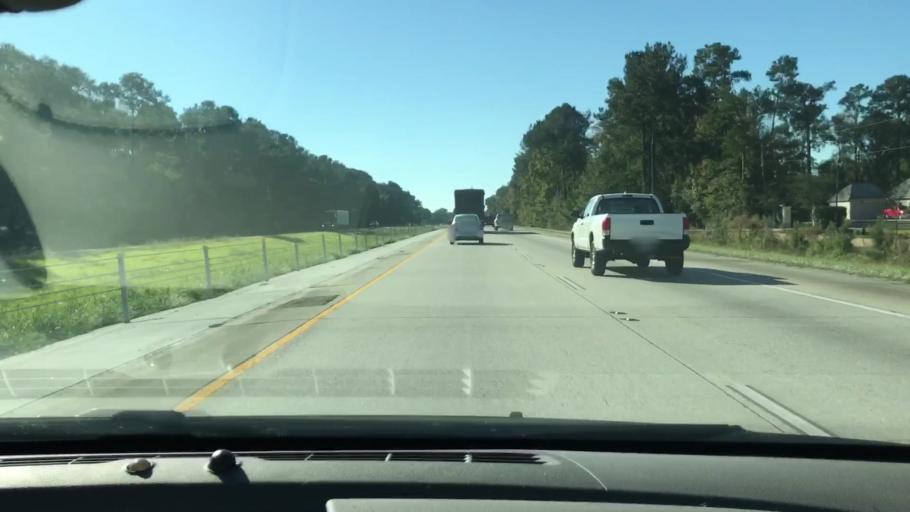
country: US
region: Louisiana
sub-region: Saint Tammany Parish
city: Pearl River
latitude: 30.3303
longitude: -89.7378
